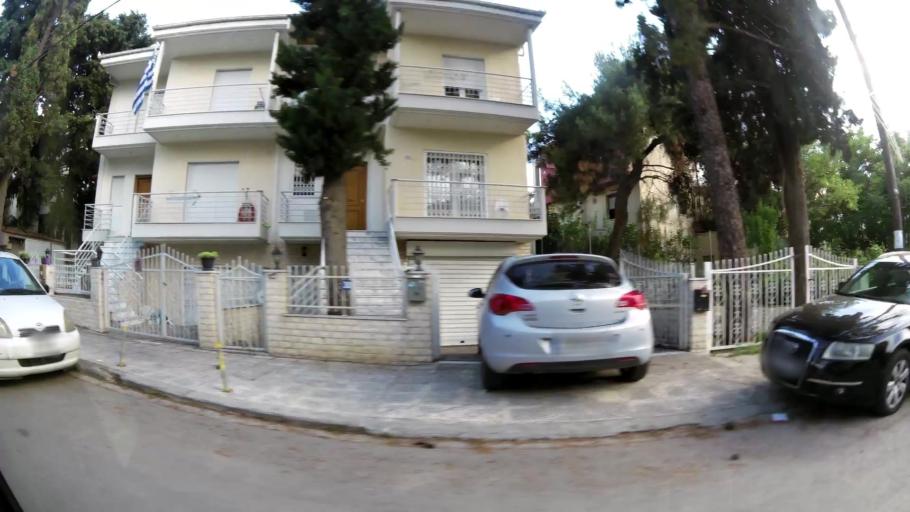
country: GR
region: Central Macedonia
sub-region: Nomos Thessalonikis
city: Pefka
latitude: 40.6565
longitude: 22.9858
